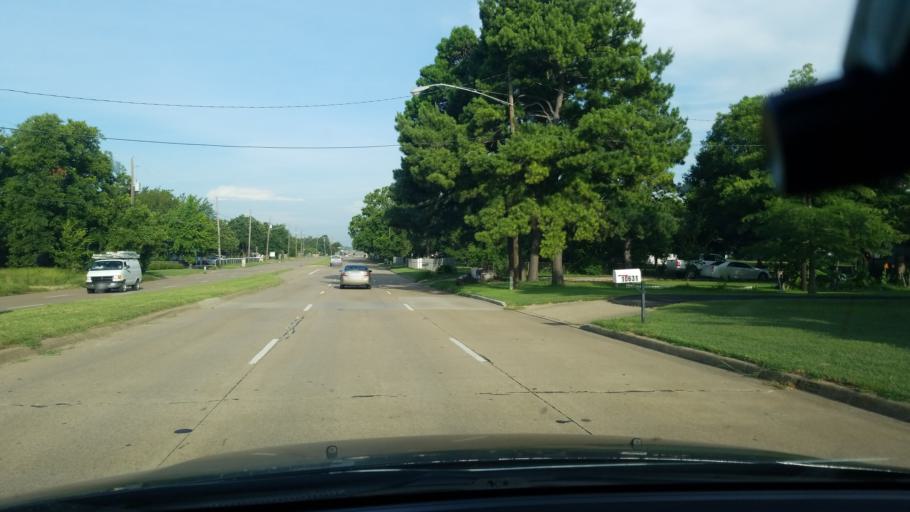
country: US
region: Texas
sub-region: Dallas County
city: Balch Springs
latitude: 32.7487
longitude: -96.6423
